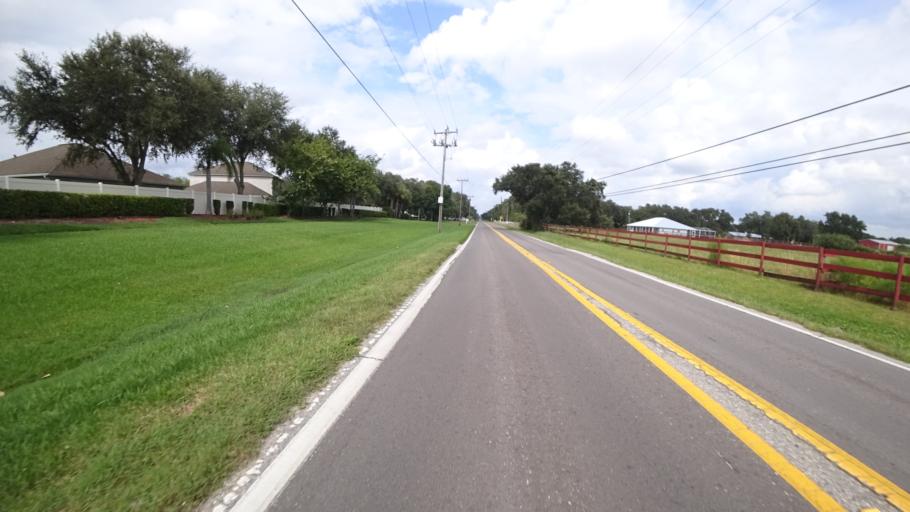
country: US
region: Florida
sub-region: Manatee County
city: Ellenton
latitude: 27.5568
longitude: -82.4788
